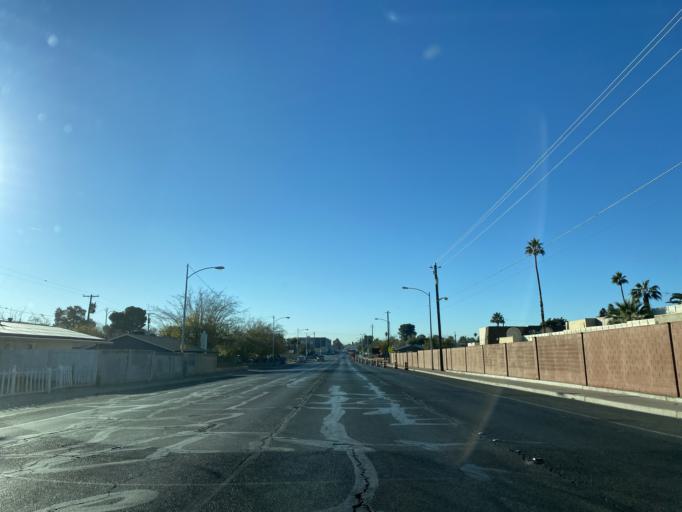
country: US
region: Nevada
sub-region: Clark County
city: Winchester
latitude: 36.1273
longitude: -115.0920
